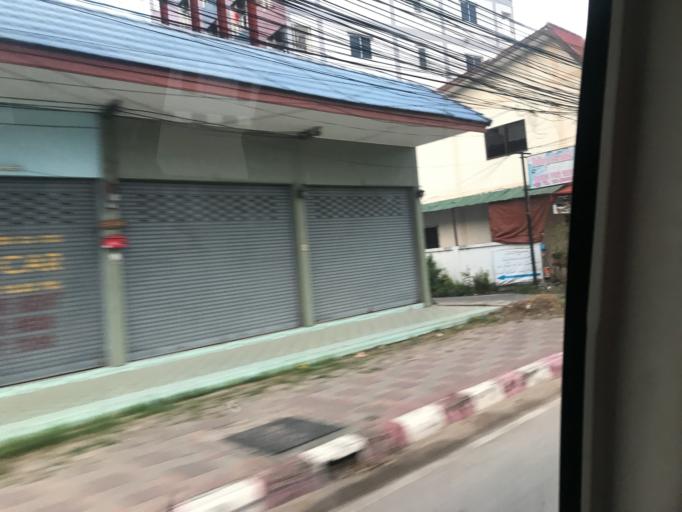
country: TH
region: Chon Buri
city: Phatthaya
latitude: 12.9203
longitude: 100.8740
